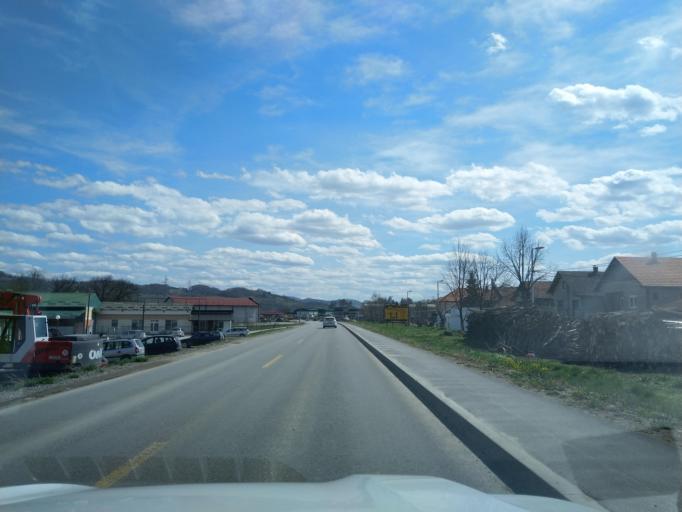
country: RS
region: Central Serbia
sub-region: Zlatiborski Okrug
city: Arilje
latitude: 43.7602
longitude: 20.0969
